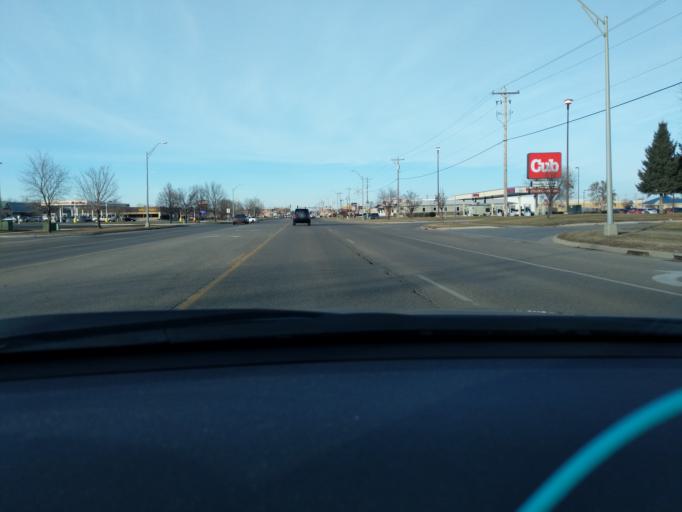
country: US
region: Minnesota
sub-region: Kandiyohi County
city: Willmar
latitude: 45.1006
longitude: -95.0426
